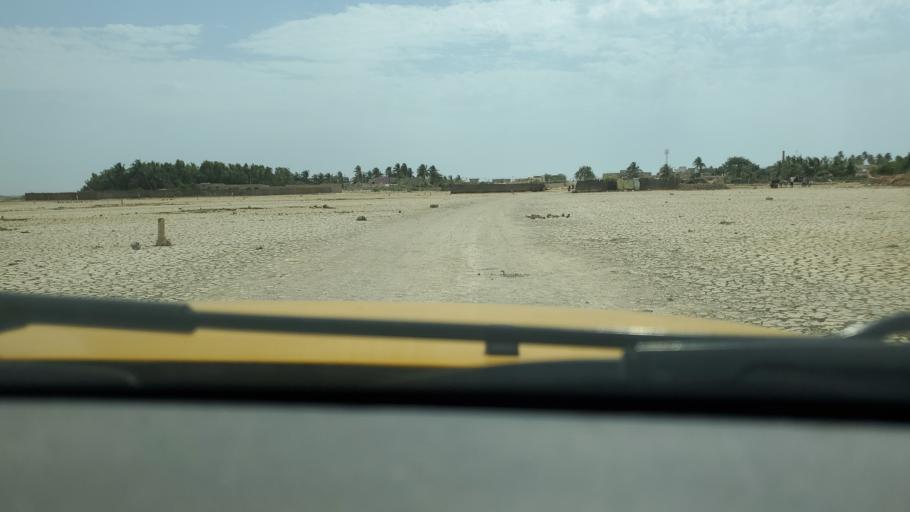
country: SN
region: Saint-Louis
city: Saint-Louis
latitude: 16.0264
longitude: -16.4700
